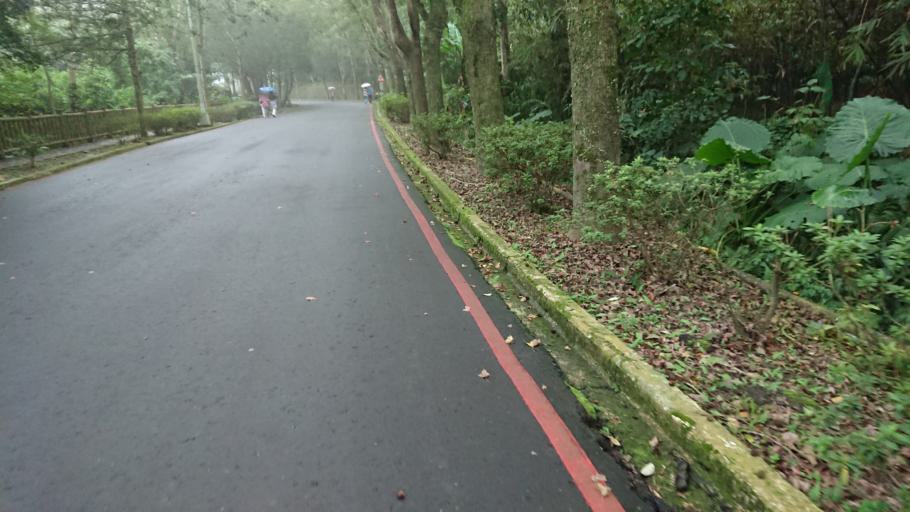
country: TW
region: Taiwan
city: Daxi
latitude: 24.8170
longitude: 121.2407
